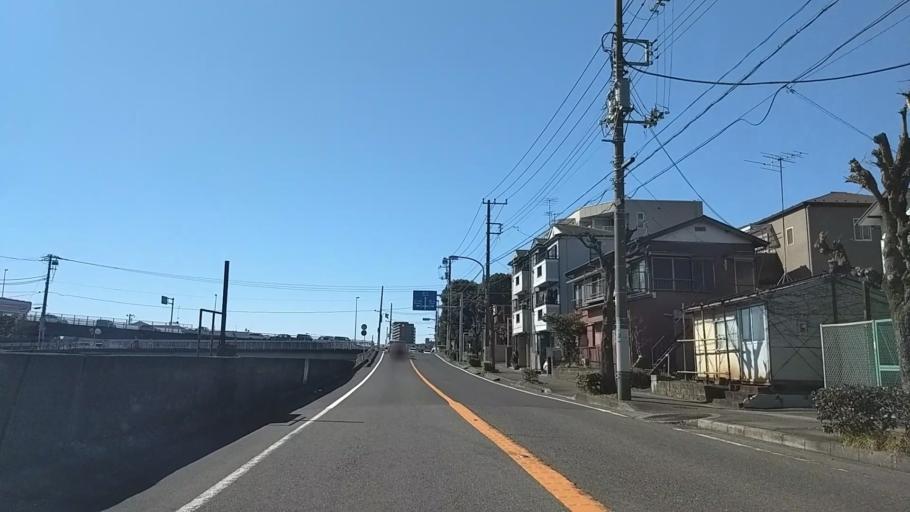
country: JP
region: Kanagawa
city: Kamakura
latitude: 35.3483
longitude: 139.5238
